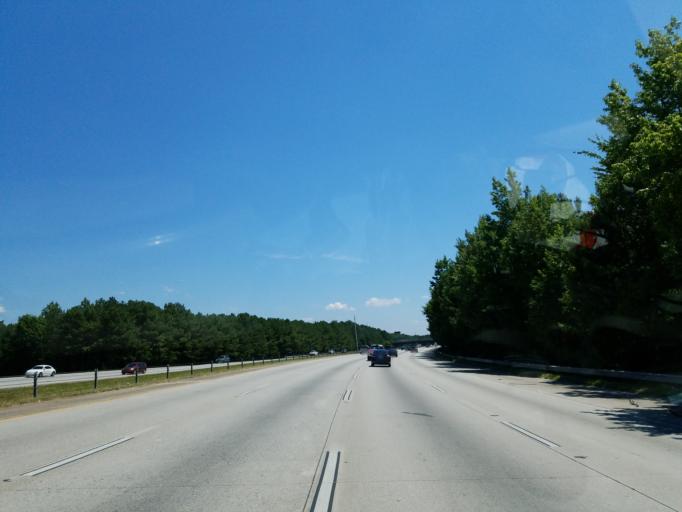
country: US
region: Georgia
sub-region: Clayton County
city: Conley
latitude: 33.6645
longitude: -84.3249
